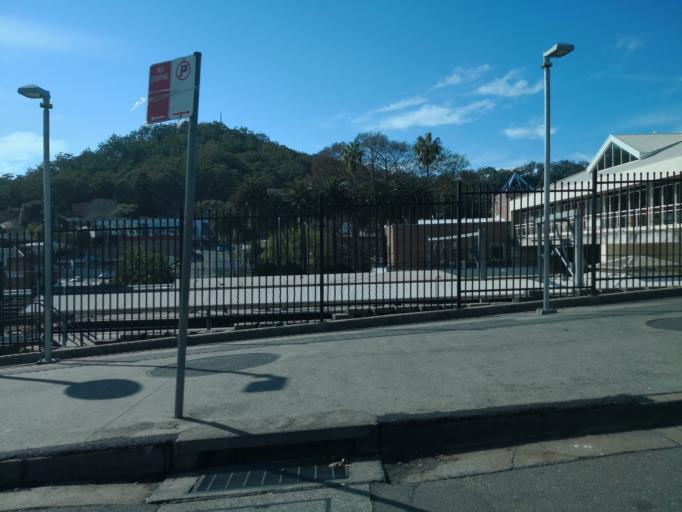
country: AU
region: New South Wales
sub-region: Gosford Shire
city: Gosford
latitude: -33.4231
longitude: 151.3413
